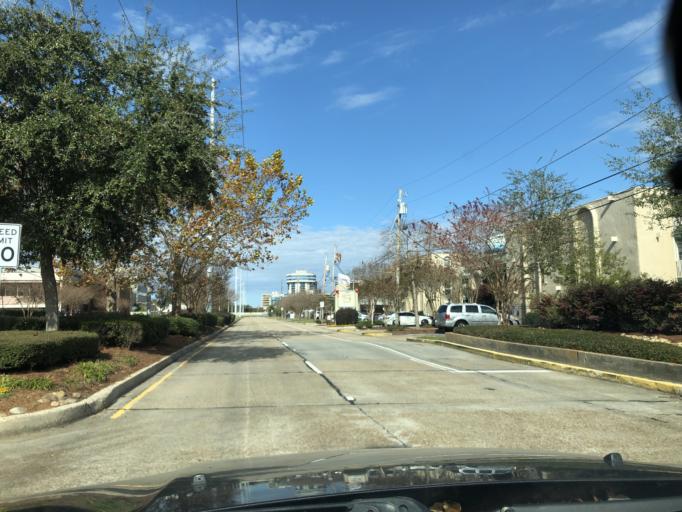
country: US
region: Louisiana
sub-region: Jefferson Parish
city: Metairie
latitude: 29.9941
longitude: -90.1598
